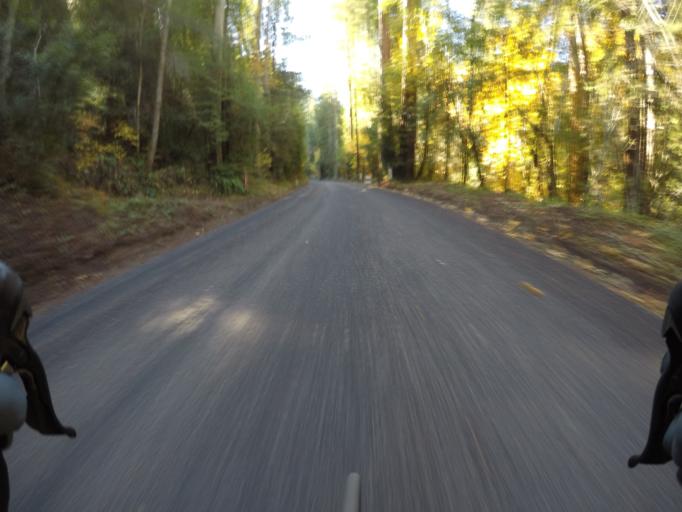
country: US
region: California
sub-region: Santa Cruz County
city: Lompico
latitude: 37.1058
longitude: -122.0232
